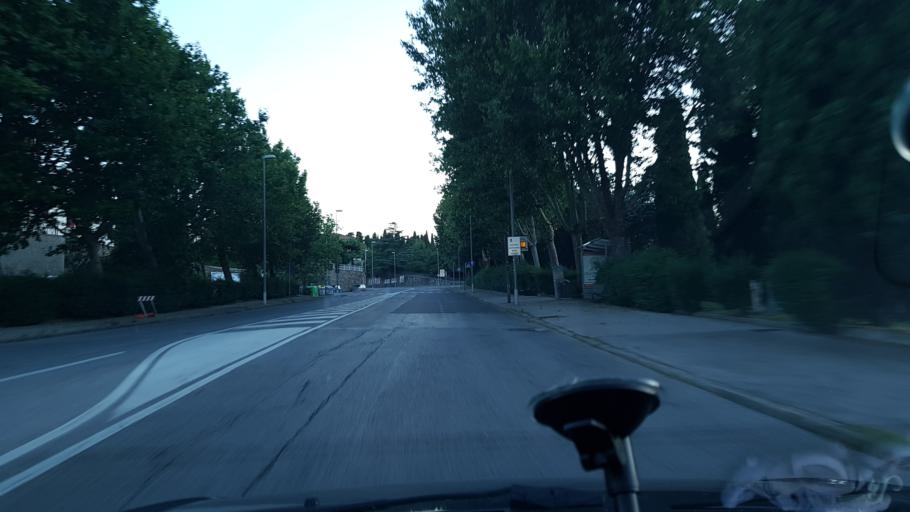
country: IT
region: Friuli Venezia Giulia
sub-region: Provincia di Trieste
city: Trieste
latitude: 45.6282
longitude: 13.7941
